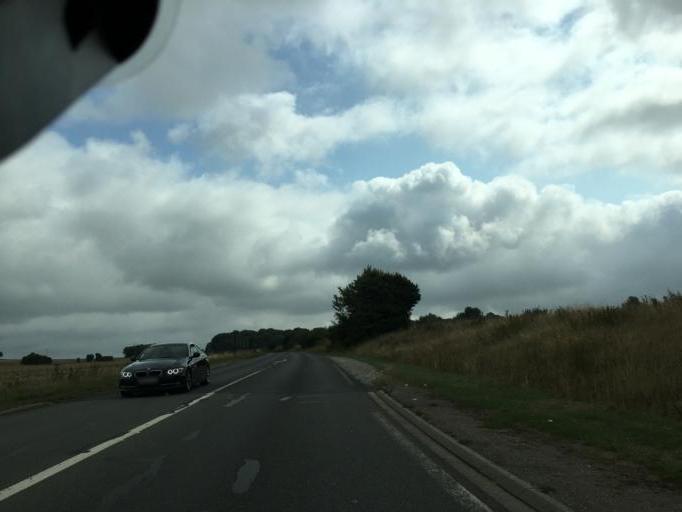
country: FR
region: Nord-Pas-de-Calais
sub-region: Departement du Pas-de-Calais
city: Rang-du-Fliers
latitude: 50.4187
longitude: 1.6561
